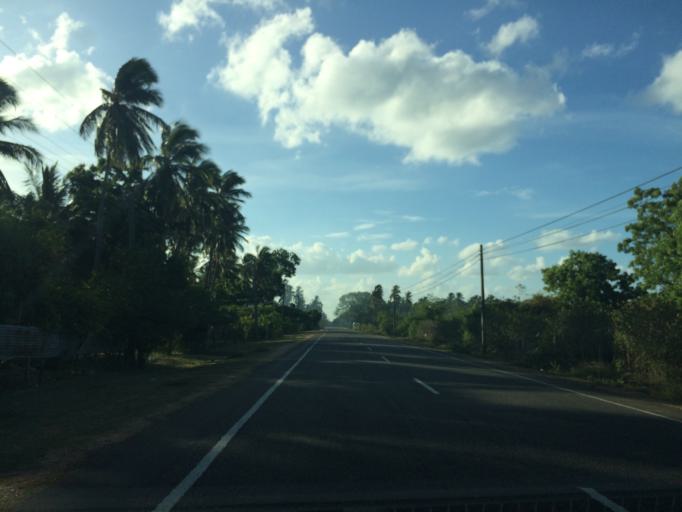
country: LK
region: Eastern Province
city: Trincomalee
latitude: 8.7102
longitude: 81.1776
